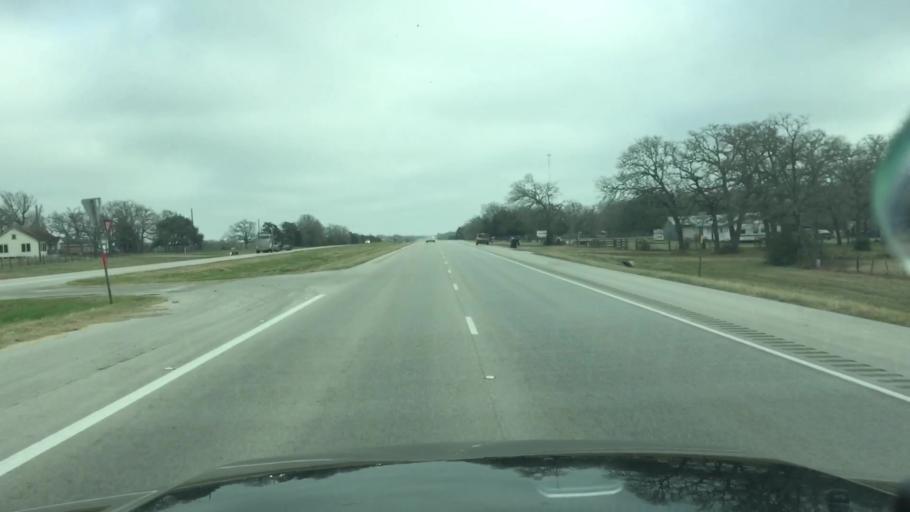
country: US
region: Texas
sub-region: Lee County
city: Giddings
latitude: 30.1461
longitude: -96.7147
